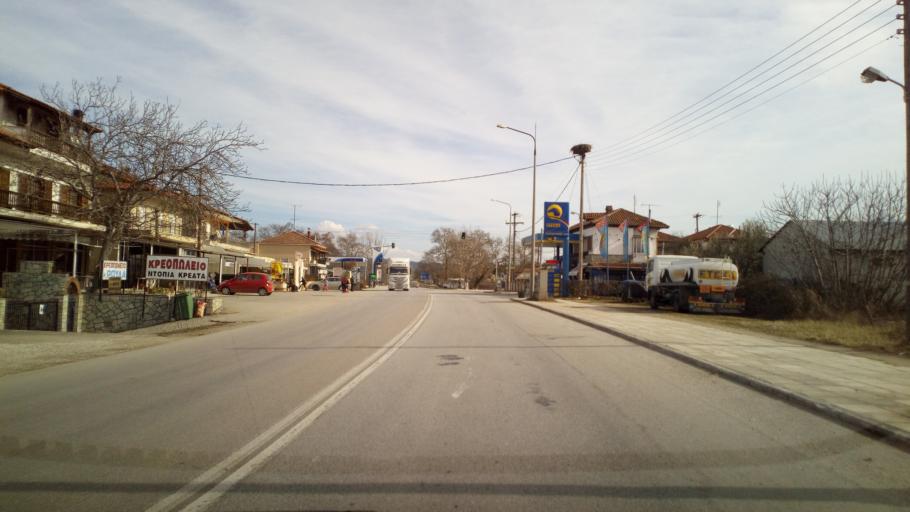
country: GR
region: Central Macedonia
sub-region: Nomos Thessalonikis
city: Gerakarou
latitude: 40.6359
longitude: 23.1904
